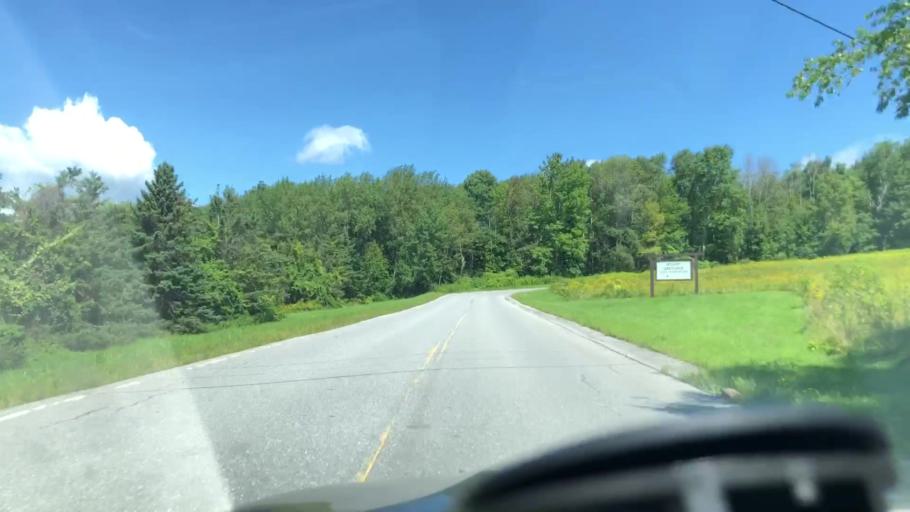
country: US
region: Massachusetts
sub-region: Berkshire County
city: Lanesborough
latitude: 42.5526
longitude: -73.2151
